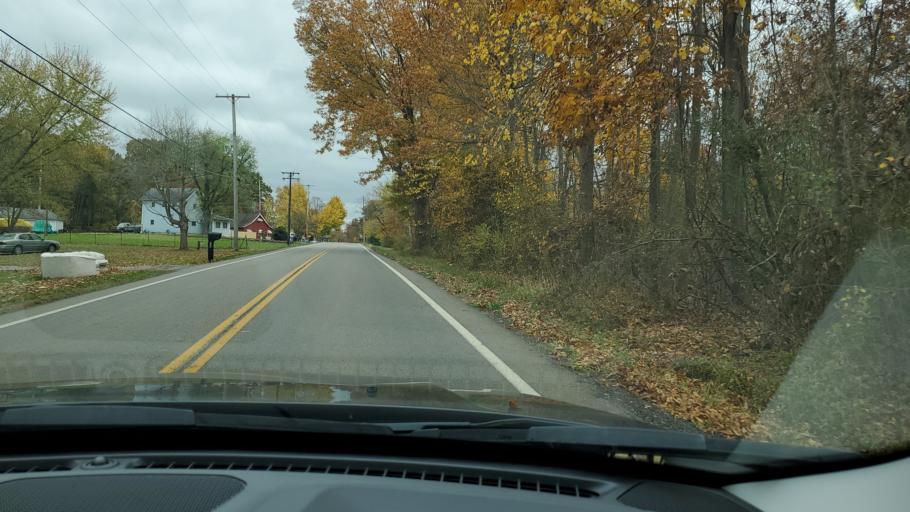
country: US
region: Ohio
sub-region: Mahoning County
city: Boardman
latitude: 40.9776
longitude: -80.6522
